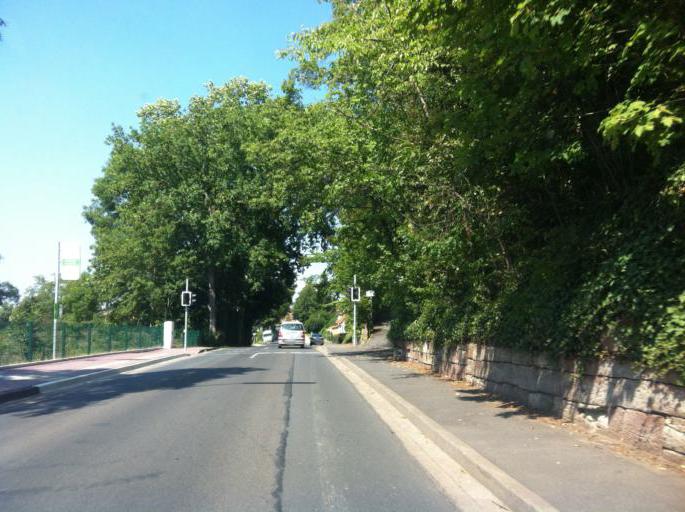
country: DE
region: Thuringia
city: Rohrberg
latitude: 51.4675
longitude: 9.9857
